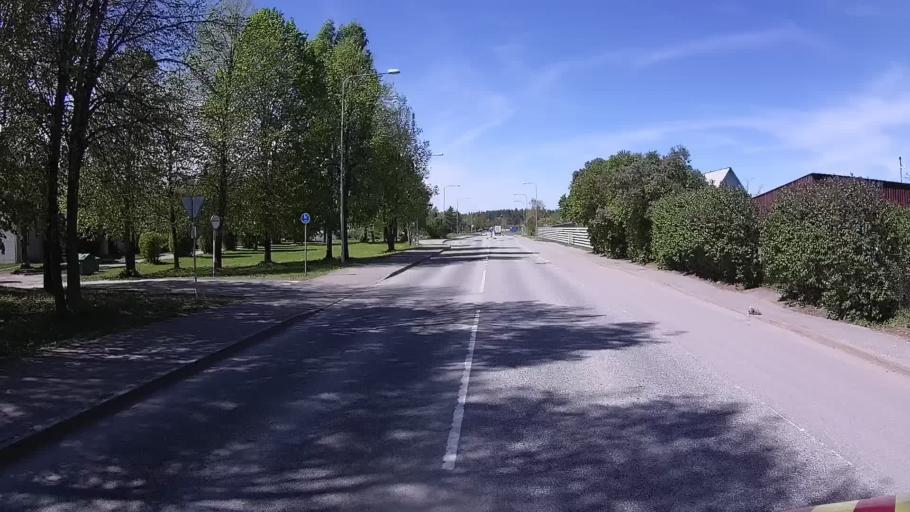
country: EE
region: Vorumaa
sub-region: Voru linn
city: Voru
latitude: 57.8143
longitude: 27.0379
